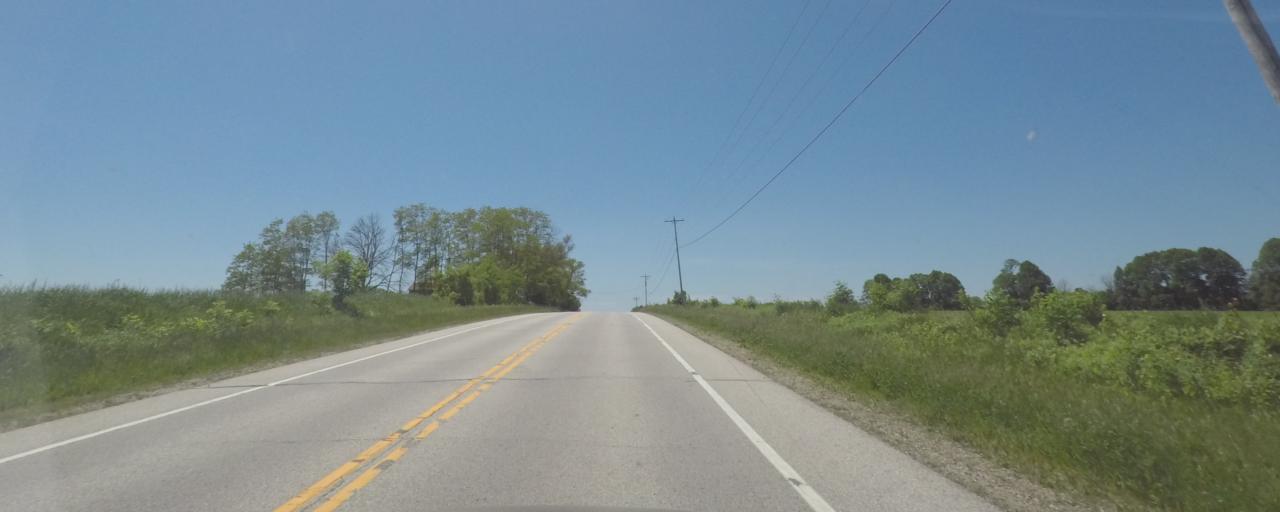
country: US
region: Wisconsin
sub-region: Ozaukee County
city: Kohler
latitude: 43.5775
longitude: -88.0576
